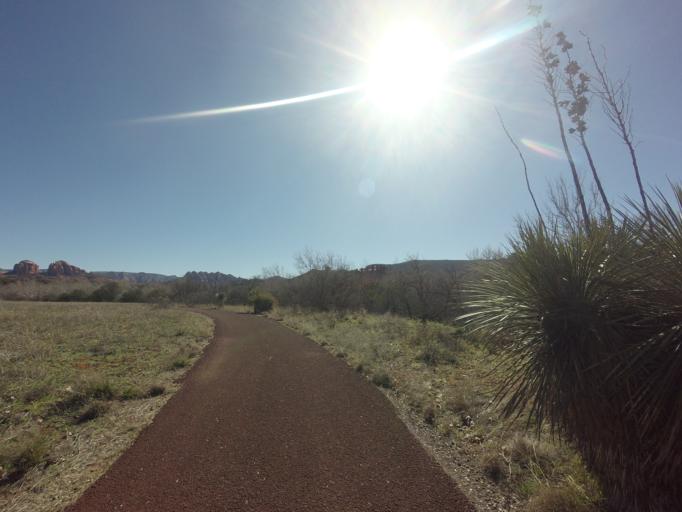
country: US
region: Arizona
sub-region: Yavapai County
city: West Sedona
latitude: 34.8100
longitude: -111.8280
